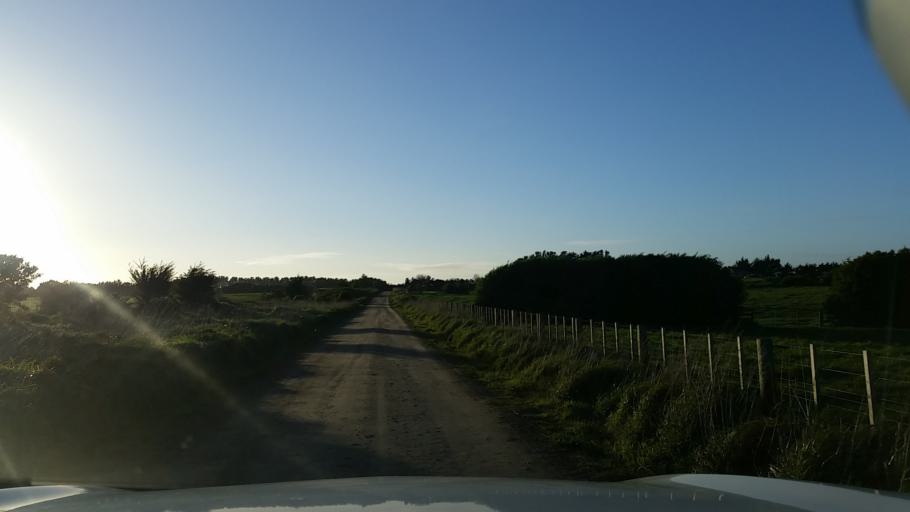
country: NZ
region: Manawatu-Wanganui
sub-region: Wanganui District
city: Wanganui
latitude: -39.8204
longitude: 174.7946
